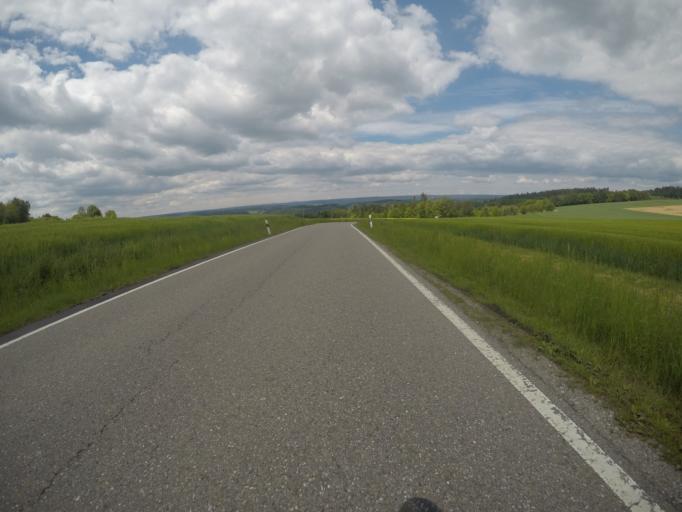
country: DE
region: Baden-Wuerttemberg
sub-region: Regierungsbezirk Stuttgart
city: Oberjettingen
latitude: 48.5836
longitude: 8.7534
